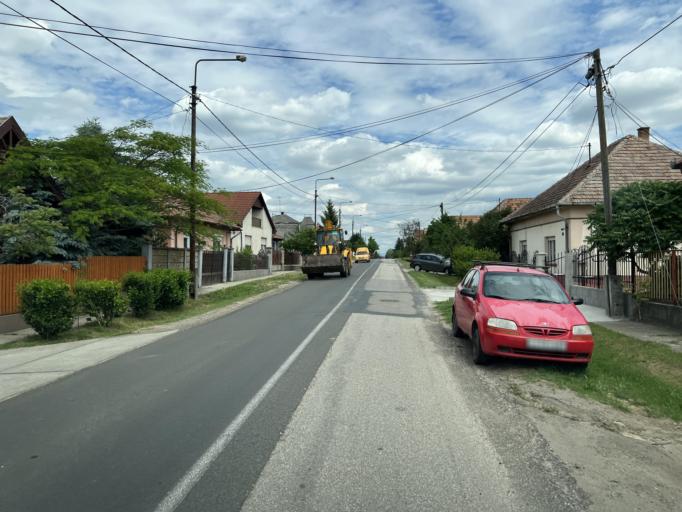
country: HU
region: Pest
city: Toalmas
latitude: 47.5043
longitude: 19.6596
